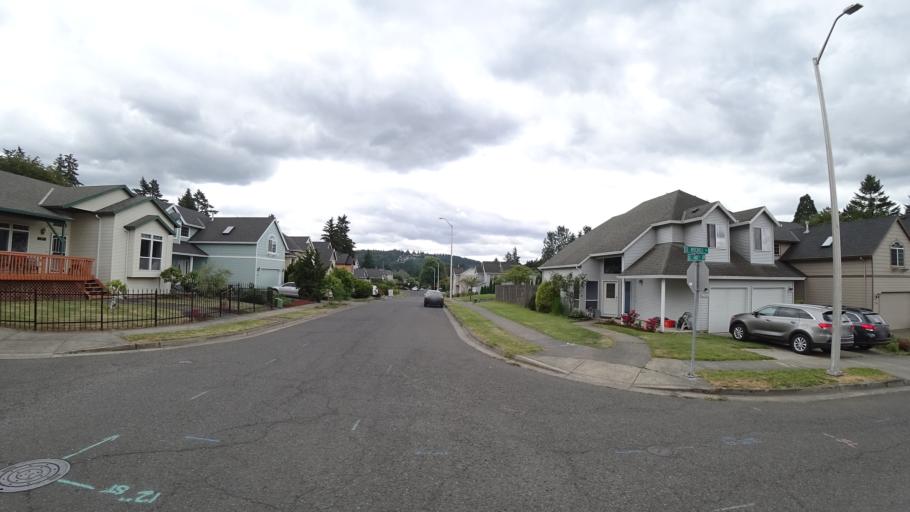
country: US
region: Oregon
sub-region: Clackamas County
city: Happy Valley
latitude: 45.4855
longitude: -122.5198
